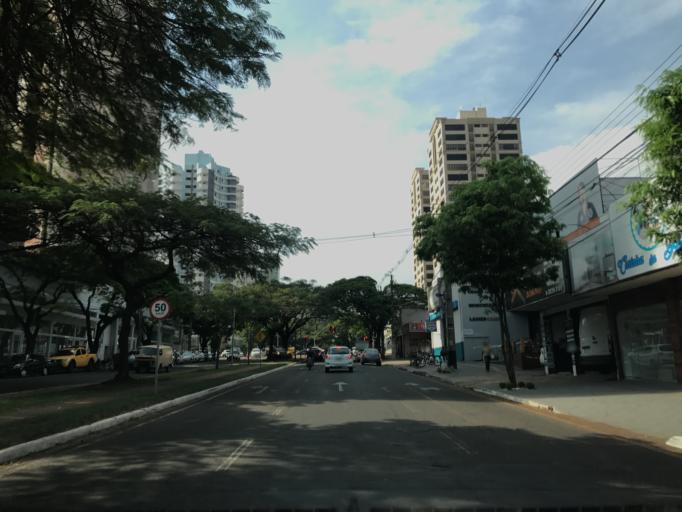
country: BR
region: Parana
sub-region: Maringa
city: Maringa
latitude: -23.4203
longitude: -51.9281
